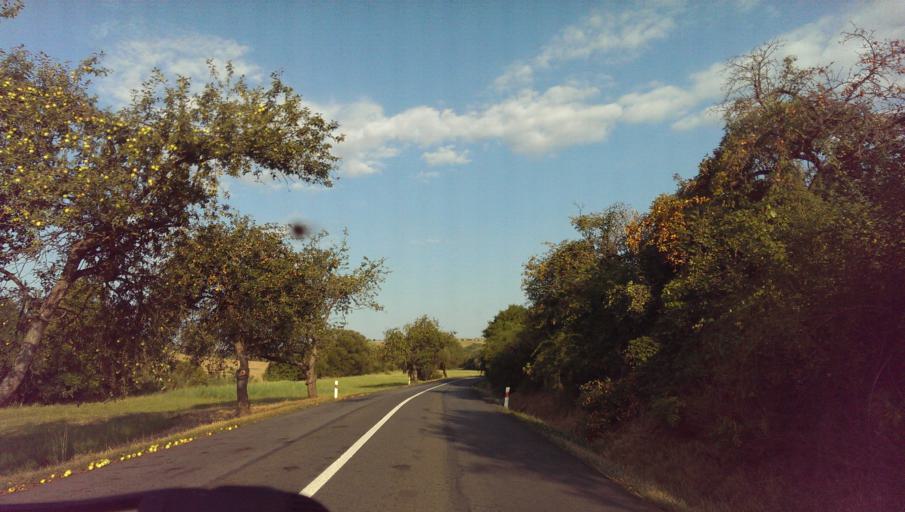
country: CZ
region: Zlin
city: Polesovice
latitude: 49.0515
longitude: 17.2947
